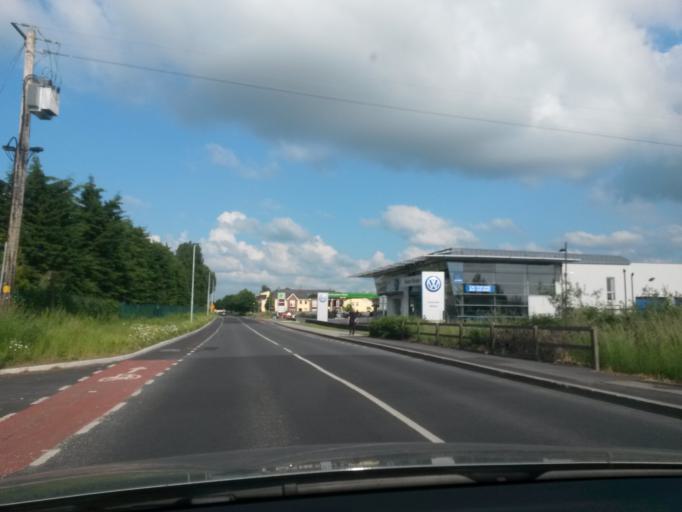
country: IE
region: Munster
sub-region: An Clar
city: Ennis
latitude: 52.8387
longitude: -8.9665
